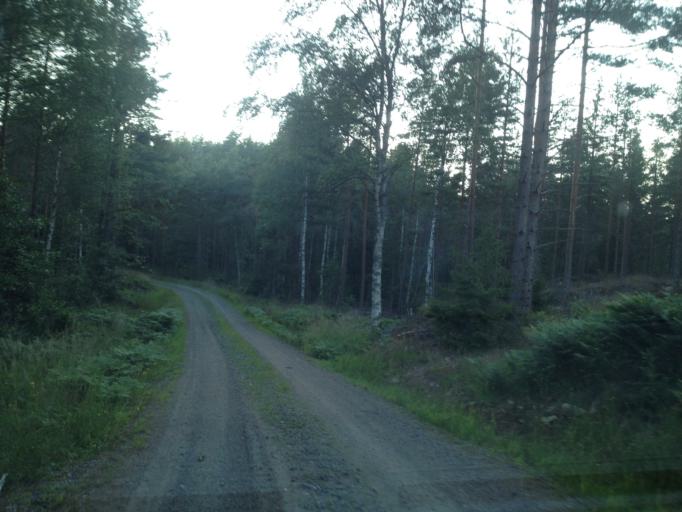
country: SE
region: Kalmar
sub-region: Vasterviks Kommun
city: Overum
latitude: 58.0005
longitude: 16.1300
